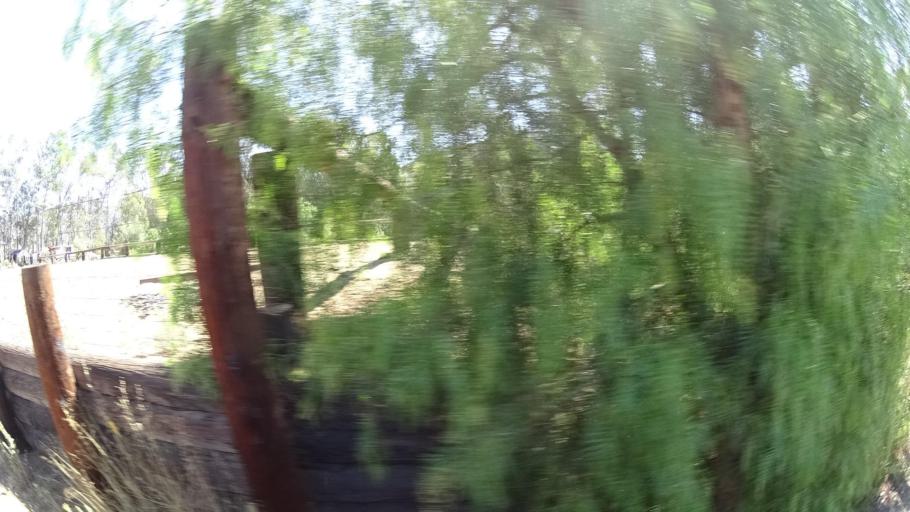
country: US
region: California
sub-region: San Diego County
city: Rainbow
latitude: 33.4318
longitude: -117.1626
